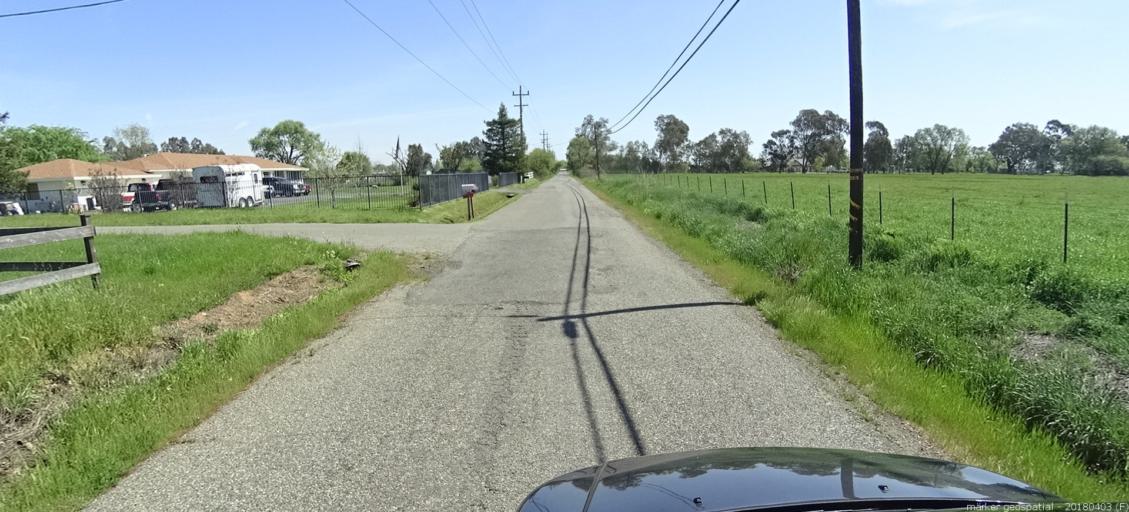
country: US
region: California
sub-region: Sacramento County
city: Wilton
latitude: 38.3952
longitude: -121.2845
